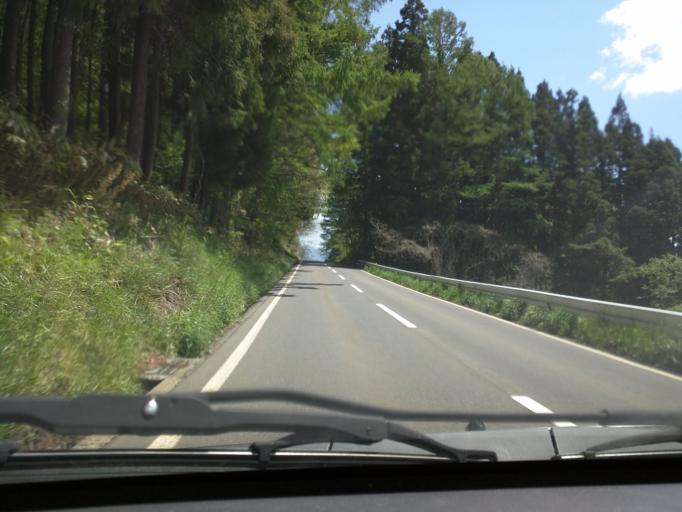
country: JP
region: Nagano
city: Nagano-shi
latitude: 36.6824
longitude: 138.1661
